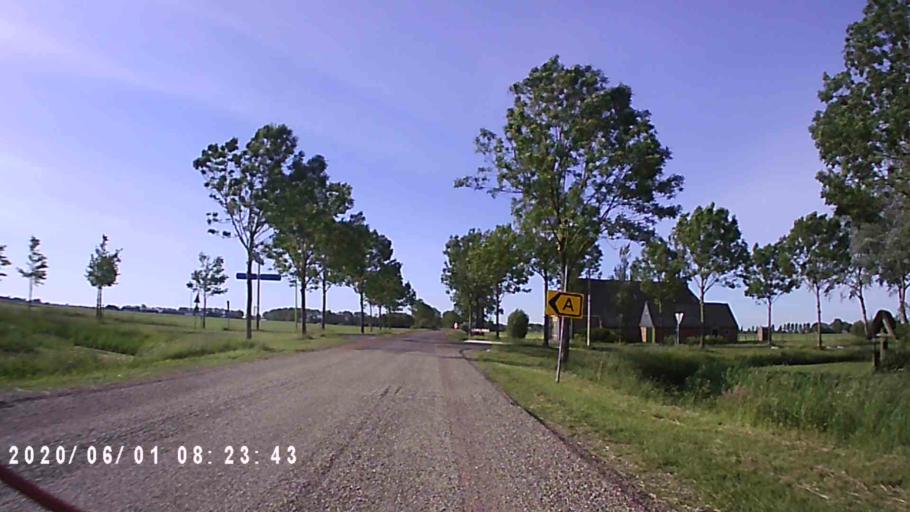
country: NL
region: Friesland
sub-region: Gemeente Ferwerderadiel
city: Burdaard
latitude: 53.3045
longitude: 5.8732
